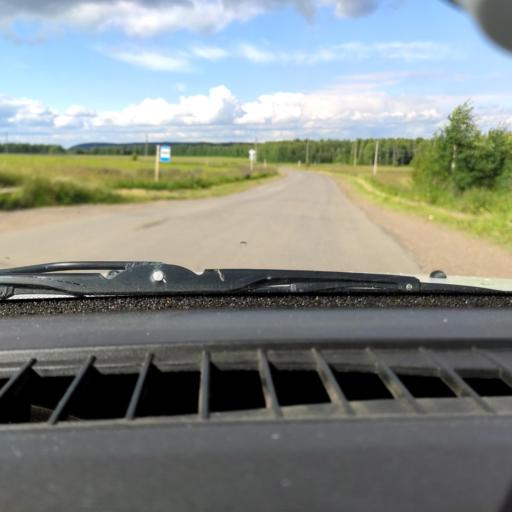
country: RU
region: Perm
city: Uinskoye
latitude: 57.1414
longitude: 56.5667
